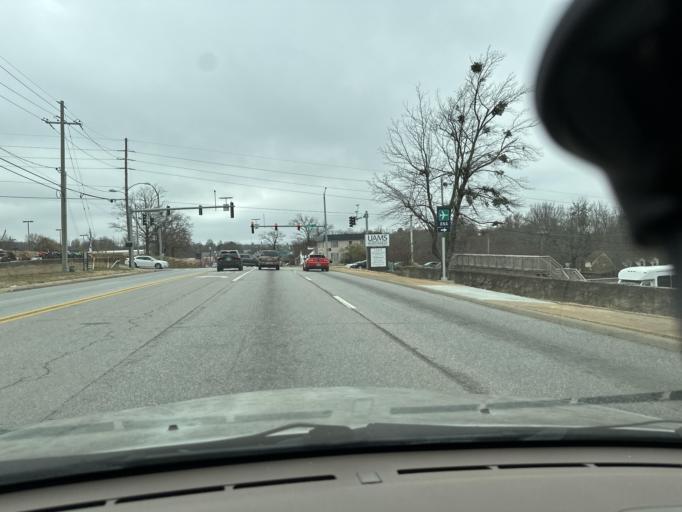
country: US
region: Arkansas
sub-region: Washington County
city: Fayetteville
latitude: 36.0778
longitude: -94.1571
